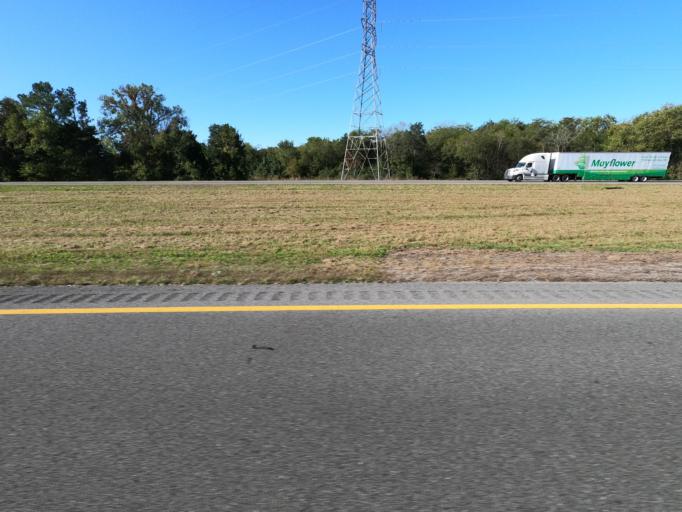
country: US
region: Tennessee
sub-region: Rutherford County
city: Plainview
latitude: 35.7517
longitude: -86.3428
